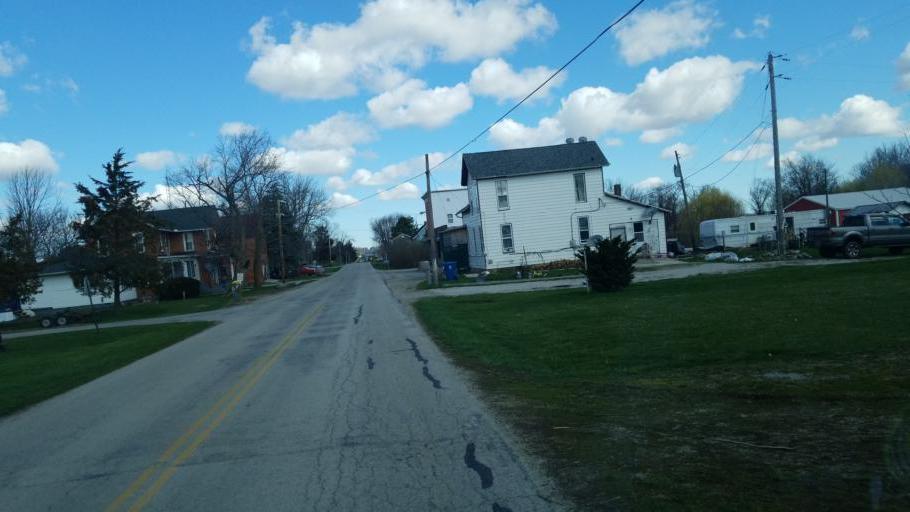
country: US
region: Ohio
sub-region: Sandusky County
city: Mount Carmel
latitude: 41.1640
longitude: -82.9381
